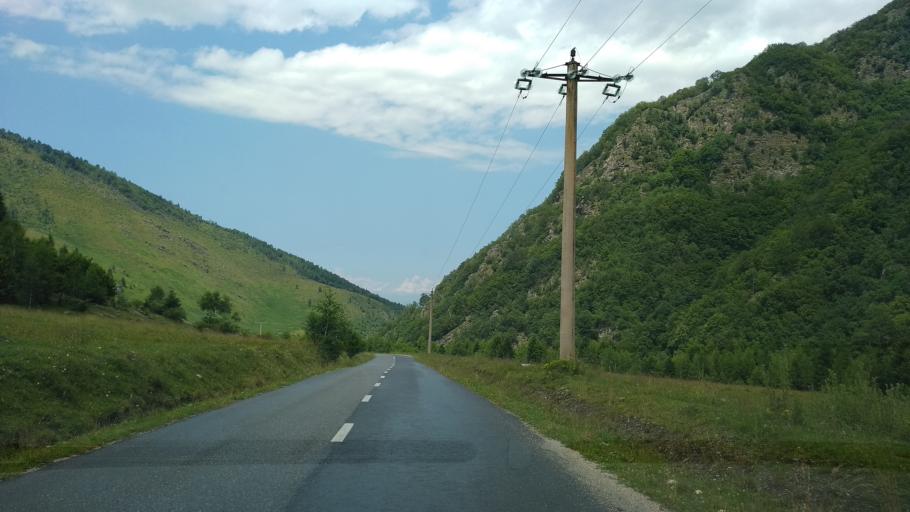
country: RO
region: Hunedoara
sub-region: Comuna Rau de Mori
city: Rau de Mori
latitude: 45.4599
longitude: 22.8982
